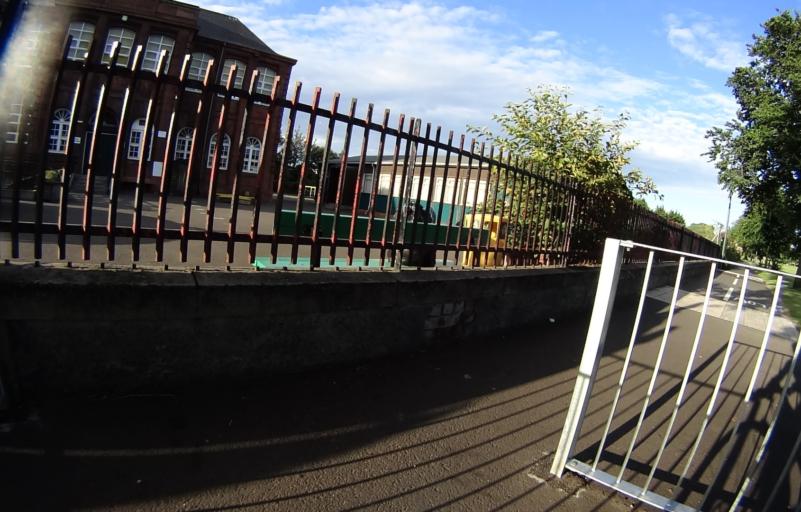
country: GB
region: Scotland
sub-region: West Lothian
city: Seafield
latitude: 55.9714
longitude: -3.1595
